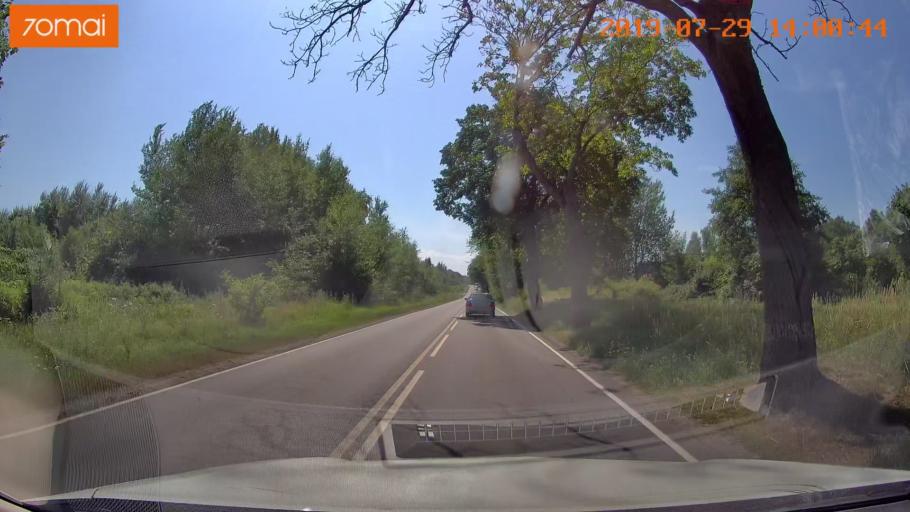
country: RU
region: Kaliningrad
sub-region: Gorod Kaliningrad
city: Baltiysk
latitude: 54.6760
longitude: 19.9262
